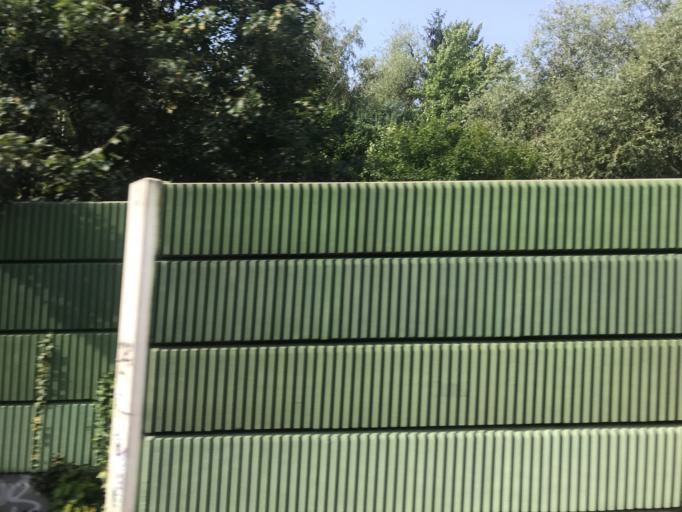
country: CZ
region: Central Bohemia
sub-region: Okres Praha-Vychod
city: Mnichovice
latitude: 49.9341
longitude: 14.7052
